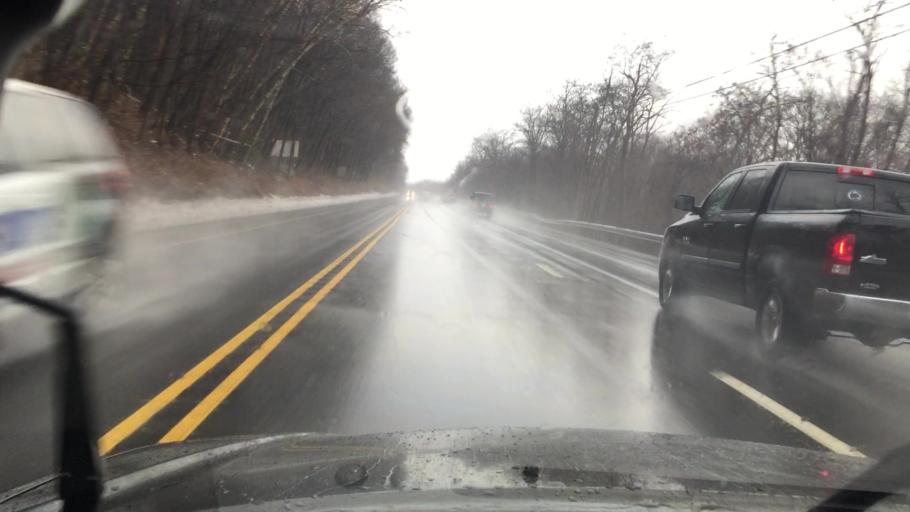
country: US
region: Pennsylvania
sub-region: Luzerne County
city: Harleigh
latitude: 41.0039
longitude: -75.9745
